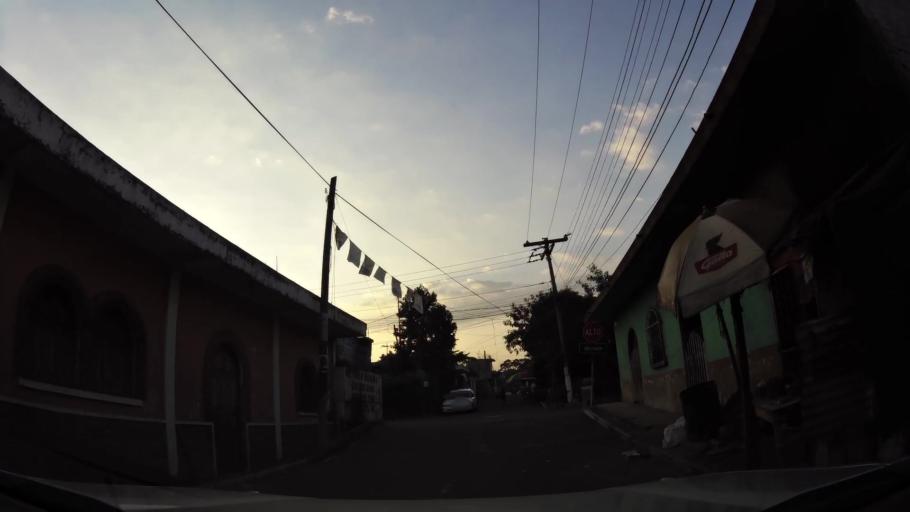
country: GT
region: Retalhuleu
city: San Sebastian
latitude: 14.5597
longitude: -91.6503
